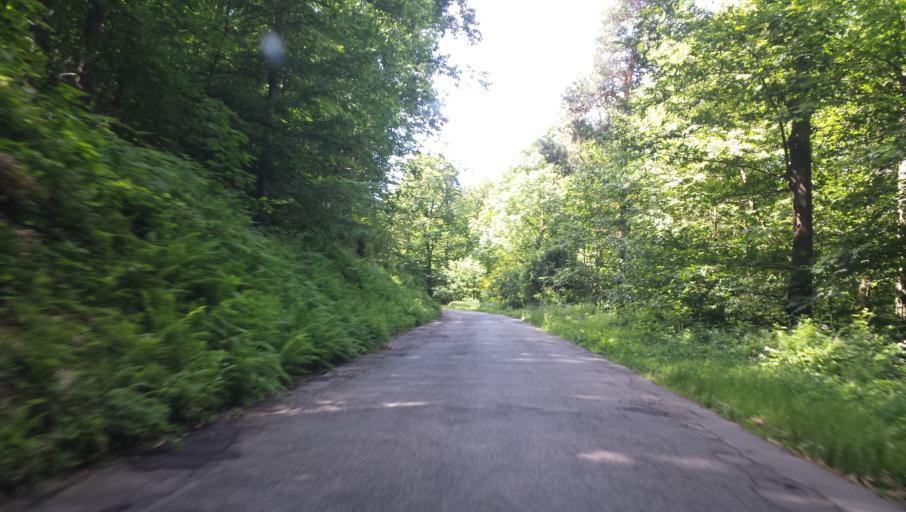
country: DE
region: Baden-Wuerttemberg
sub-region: Karlsruhe Region
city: Heidelberg
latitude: 49.4293
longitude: 8.7009
